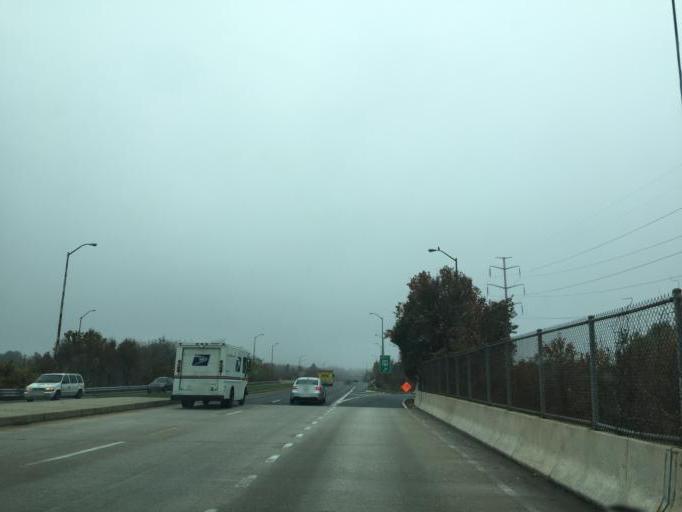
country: US
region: Maryland
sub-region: Howard County
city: Riverside
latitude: 39.2011
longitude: -76.8570
